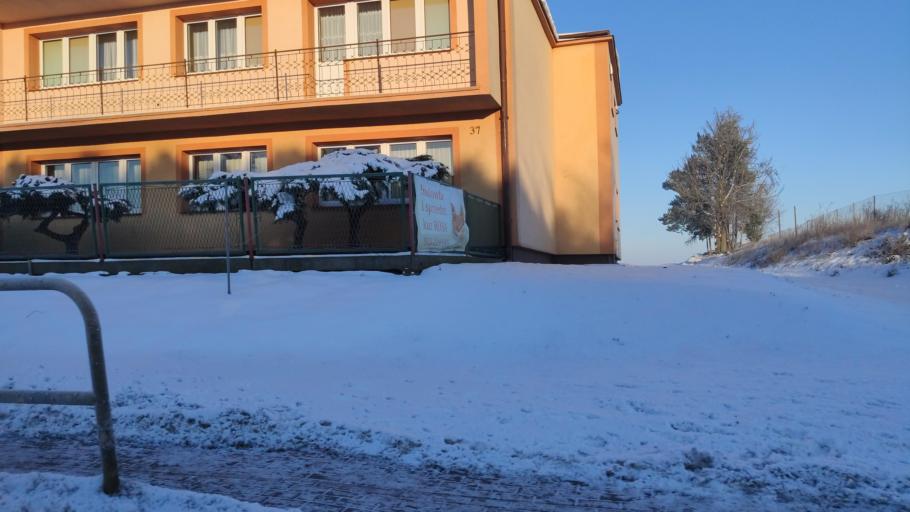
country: PL
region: Kujawsko-Pomorskie
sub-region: Powiat zninski
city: Znin
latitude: 52.8552
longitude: 17.7558
